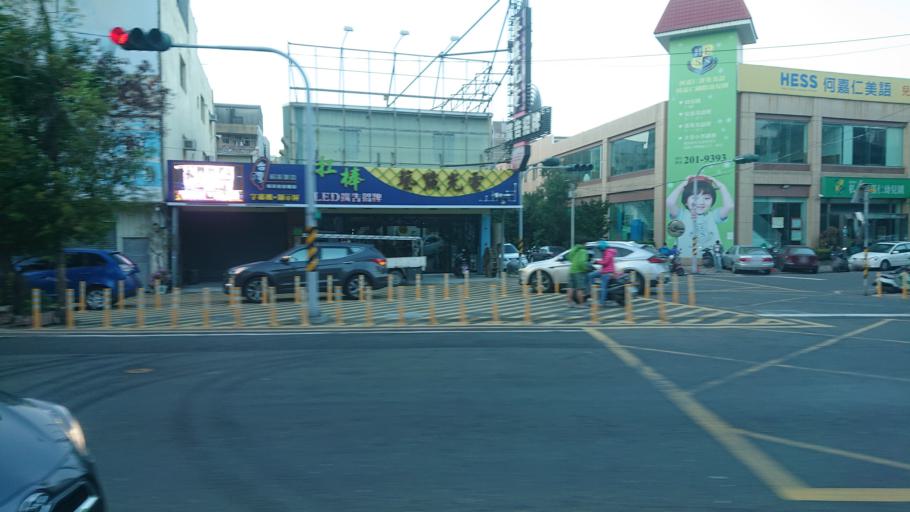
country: TW
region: Taiwan
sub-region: Tainan
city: Tainan
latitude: 23.0131
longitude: 120.2292
